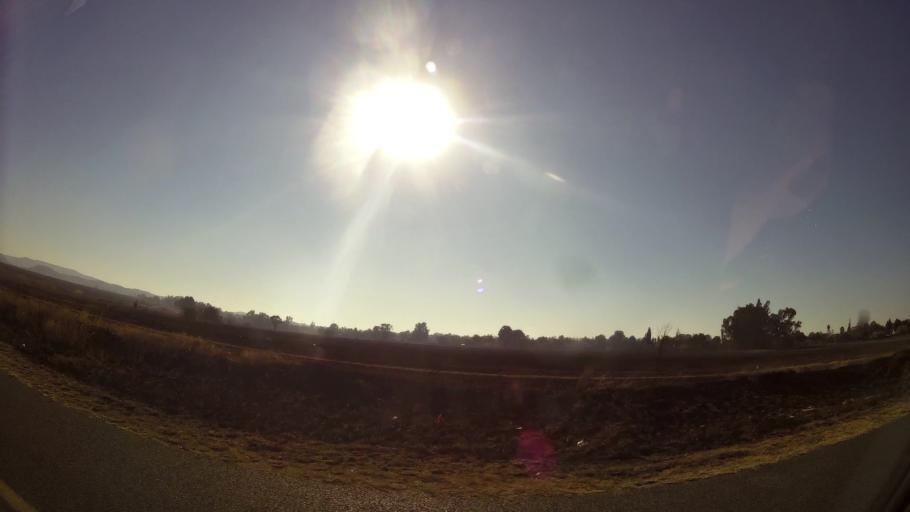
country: ZA
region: Gauteng
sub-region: City of Johannesburg Metropolitan Municipality
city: Johannesburg
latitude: -26.3336
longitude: 28.0786
